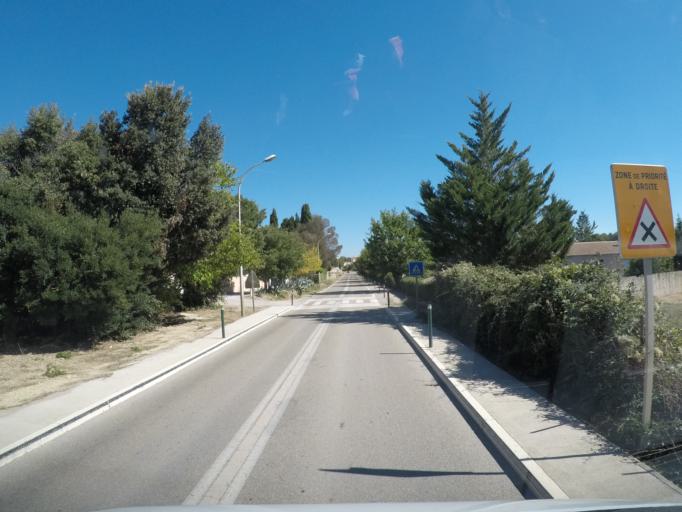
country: FR
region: Languedoc-Roussillon
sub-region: Departement de l'Herault
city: Saint-Martin-de-Londres
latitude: 43.7418
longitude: 3.6989
